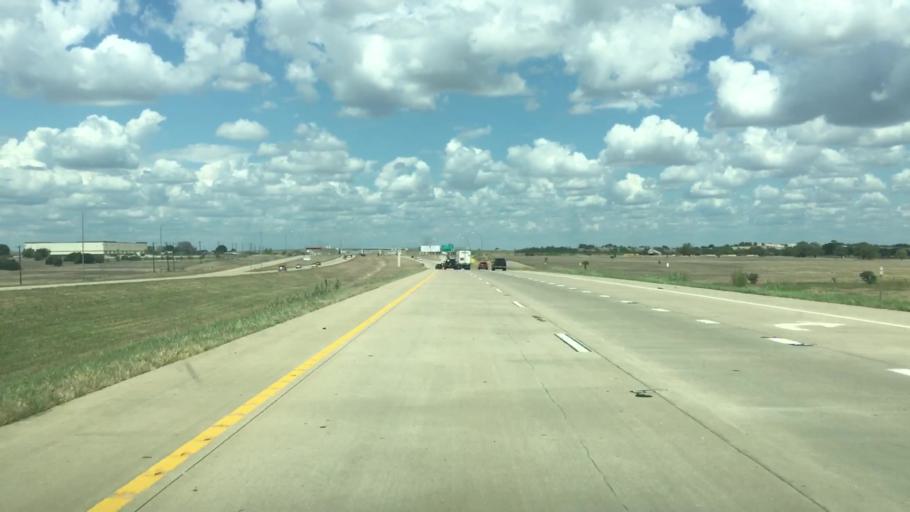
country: US
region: Texas
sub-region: Williamson County
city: Hutto
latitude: 30.5775
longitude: -97.5852
